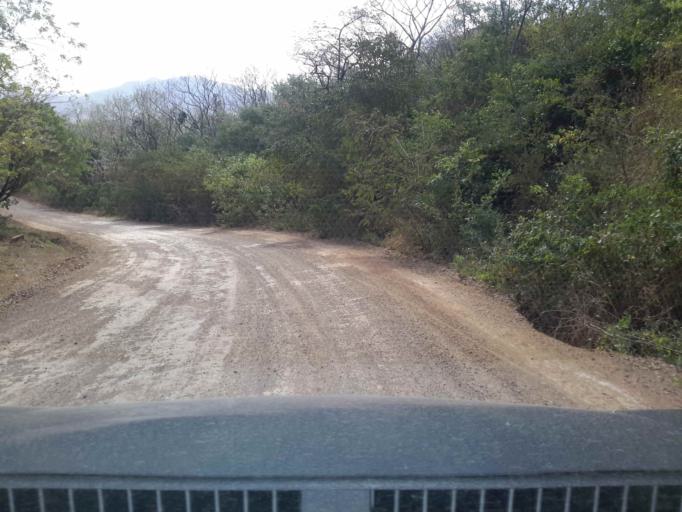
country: NI
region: Rivas
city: San Juan del Sur
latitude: 11.2194
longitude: -85.8150
